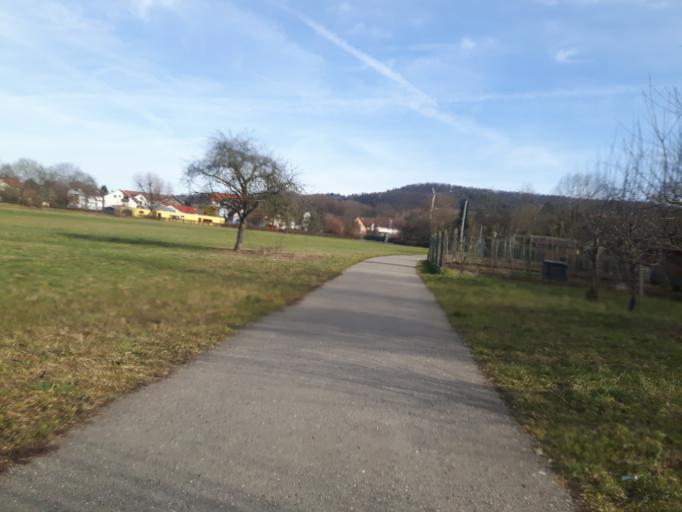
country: DE
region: Baden-Wuerttemberg
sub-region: Regierungsbezirk Stuttgart
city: Lowenstein
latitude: 49.1393
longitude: 9.3989
